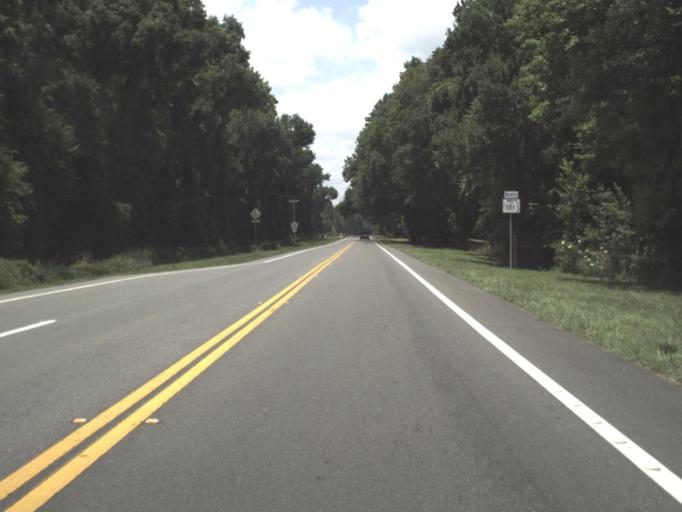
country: US
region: Florida
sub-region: Alachua County
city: Archer
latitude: 29.5290
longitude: -82.4045
